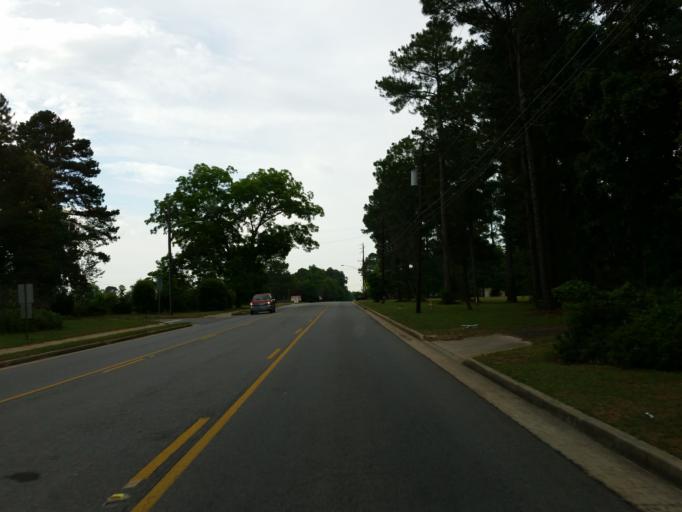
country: US
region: Georgia
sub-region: Dooly County
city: Vienna
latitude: 32.1019
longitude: -83.7986
